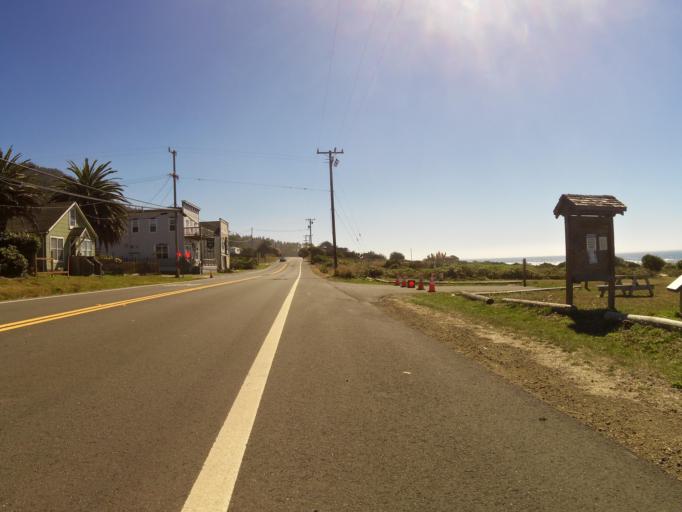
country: US
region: California
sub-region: Mendocino County
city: Fort Bragg
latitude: 39.6379
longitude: -123.7850
